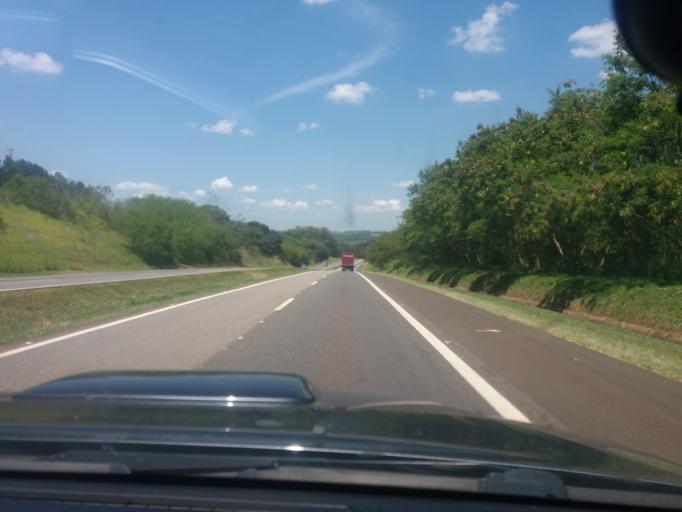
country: BR
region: Sao Paulo
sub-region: Tatui
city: Tatui
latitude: -23.3672
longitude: -47.9067
